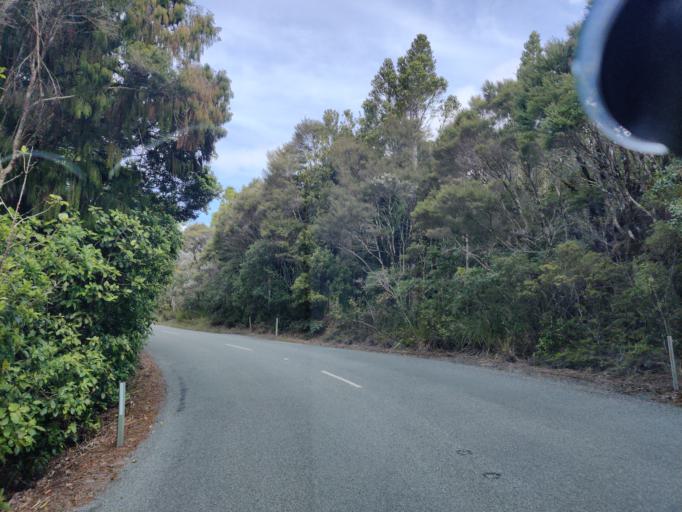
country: NZ
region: Northland
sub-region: Far North District
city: Waimate North
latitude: -35.6086
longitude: 173.5390
